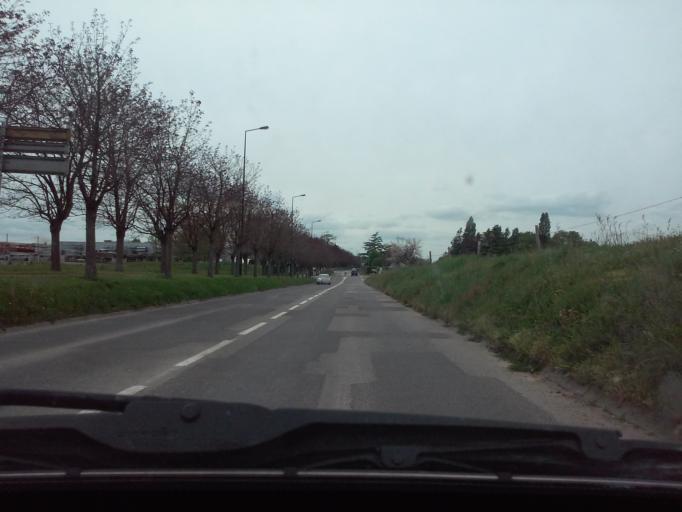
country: FR
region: Brittany
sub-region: Departement d'Ille-et-Vilaine
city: Le Rheu
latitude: 48.0974
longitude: -1.7796
